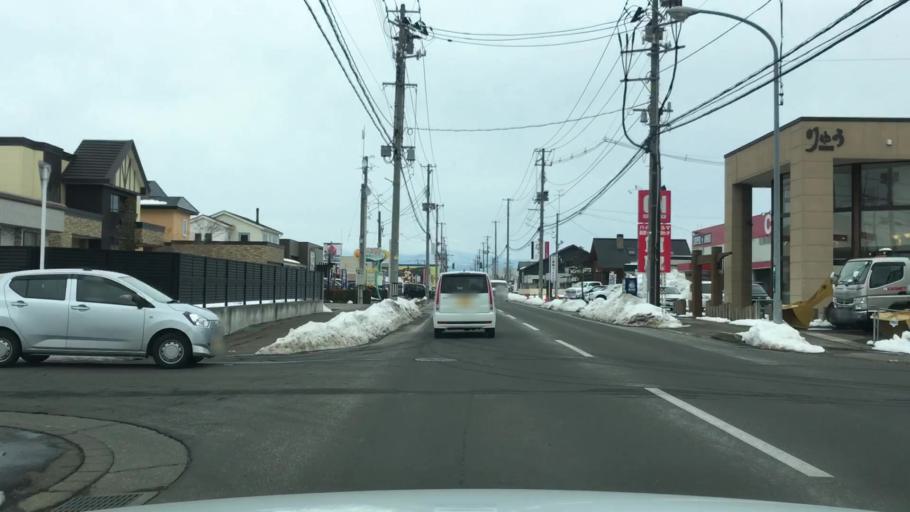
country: JP
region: Aomori
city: Hirosaki
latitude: 40.6017
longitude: 140.5093
